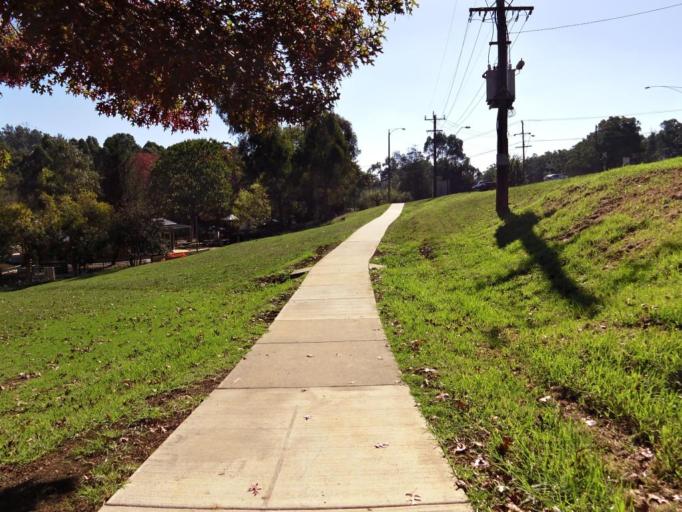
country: AU
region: Victoria
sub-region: Cardinia
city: Cockatoo
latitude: -37.9364
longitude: 145.4913
